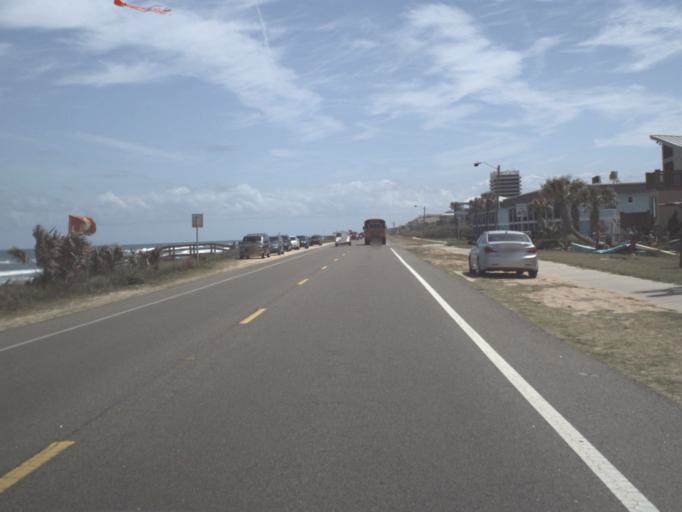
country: US
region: Florida
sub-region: Flagler County
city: Flagler Beach
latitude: 29.5020
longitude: -81.1377
